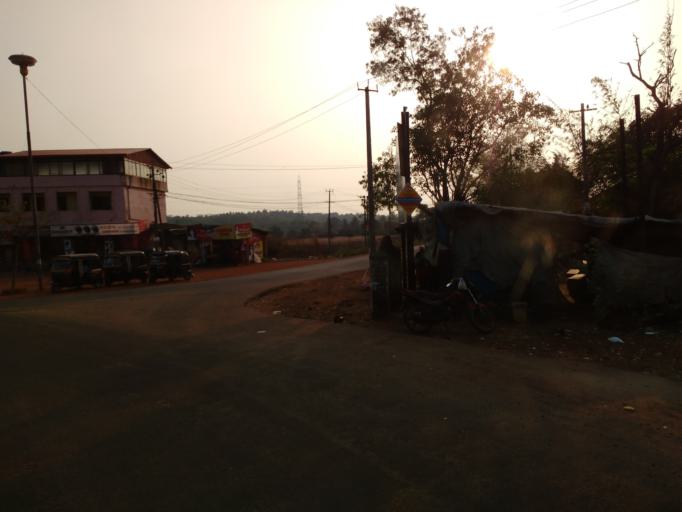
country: IN
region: Karnataka
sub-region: Dakshina Kannada
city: Mangalore
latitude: 12.9232
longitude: 74.8978
